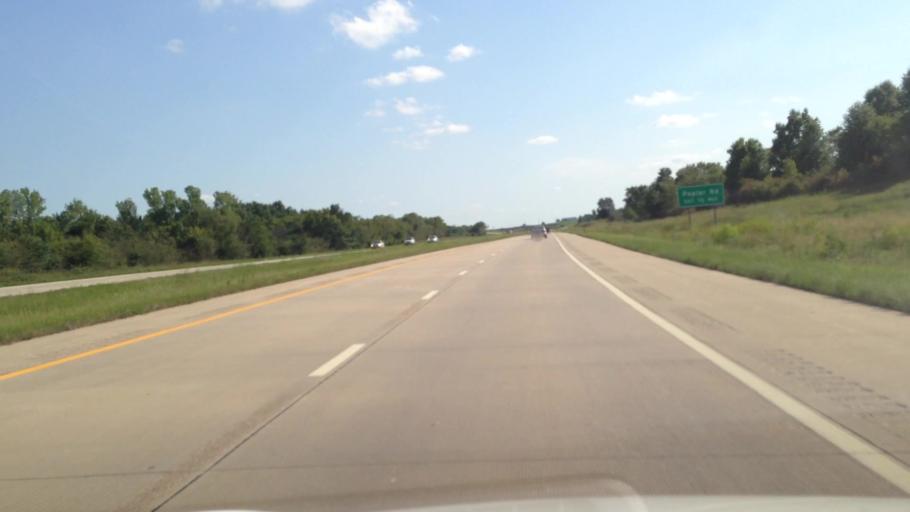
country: US
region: Kansas
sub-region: Bourbon County
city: Fort Scott
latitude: 37.9045
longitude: -94.7035
